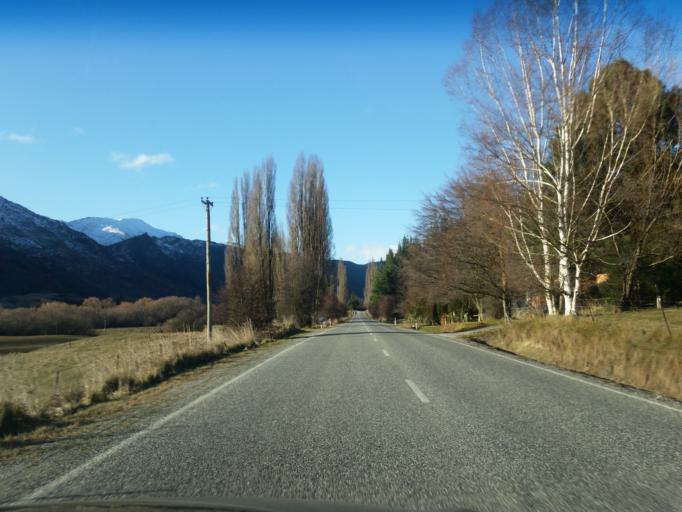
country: NZ
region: Otago
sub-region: Queenstown-Lakes District
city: Arrowtown
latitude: -44.9588
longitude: 168.7281
